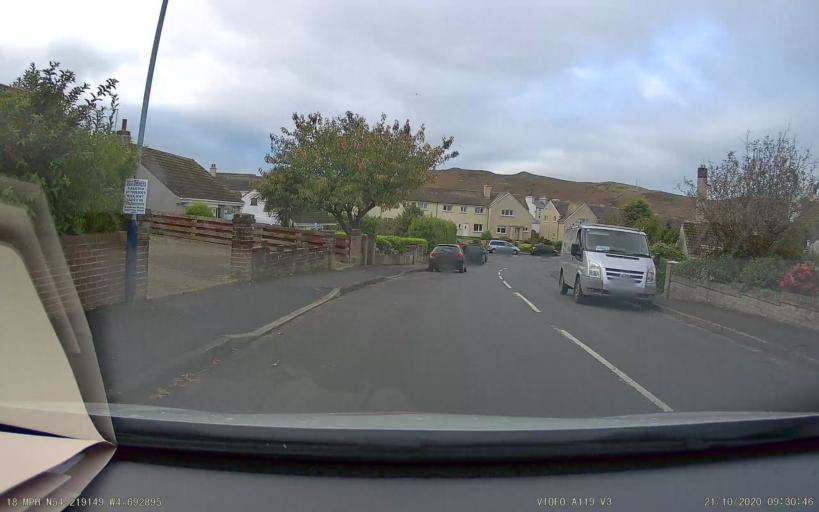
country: IM
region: Port Erin
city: Port Erin
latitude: 54.2191
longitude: -4.6932
